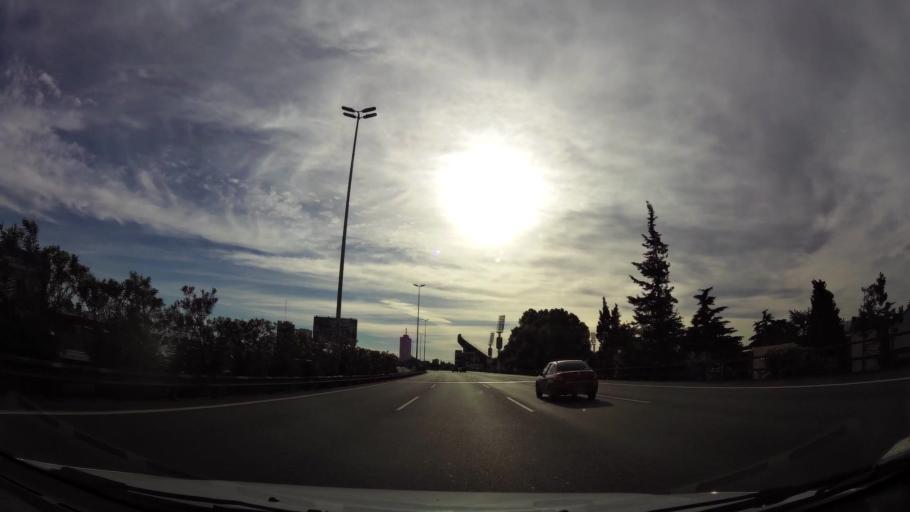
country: AR
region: Buenos Aires F.D.
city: Villa Santa Rita
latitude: -34.6355
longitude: -58.5163
